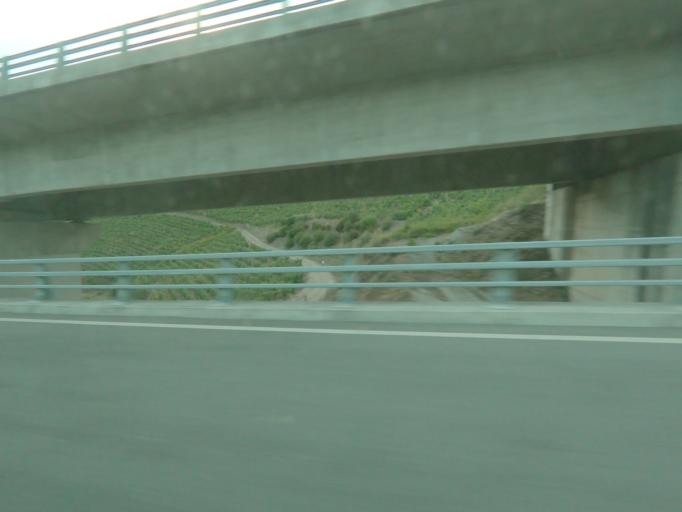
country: PT
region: Vila Real
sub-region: Peso da Regua
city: Peso da Regua
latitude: 41.1760
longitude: -7.7507
